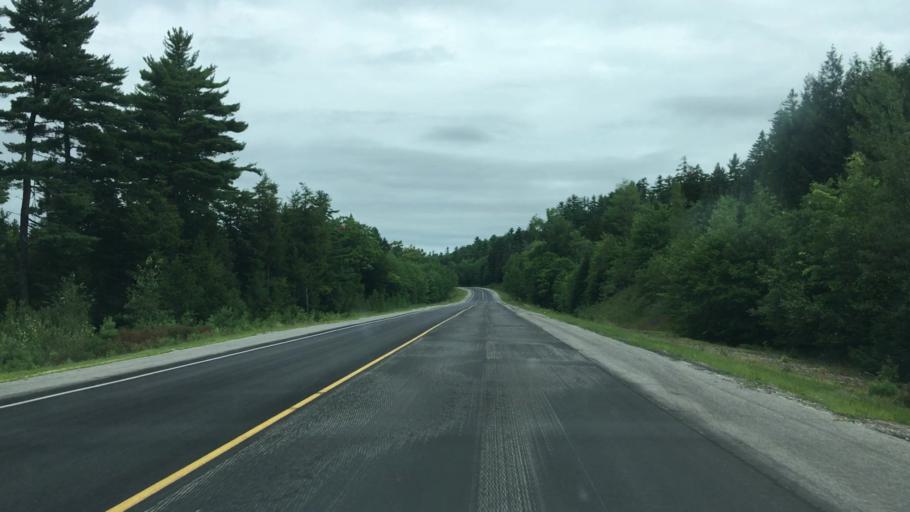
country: US
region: Maine
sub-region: Washington County
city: Cherryfield
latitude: 44.8944
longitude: -67.8560
